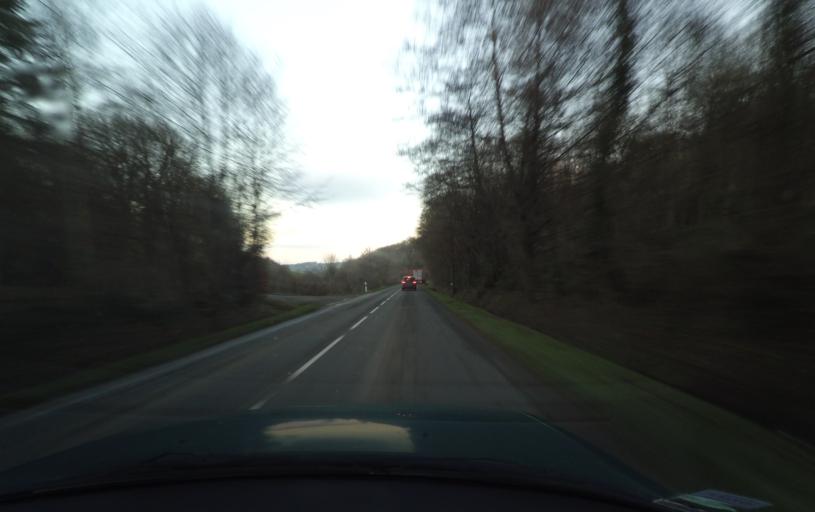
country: FR
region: Pays de la Loire
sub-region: Departement de la Mayenne
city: Bais
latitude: 48.2408
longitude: -0.3677
